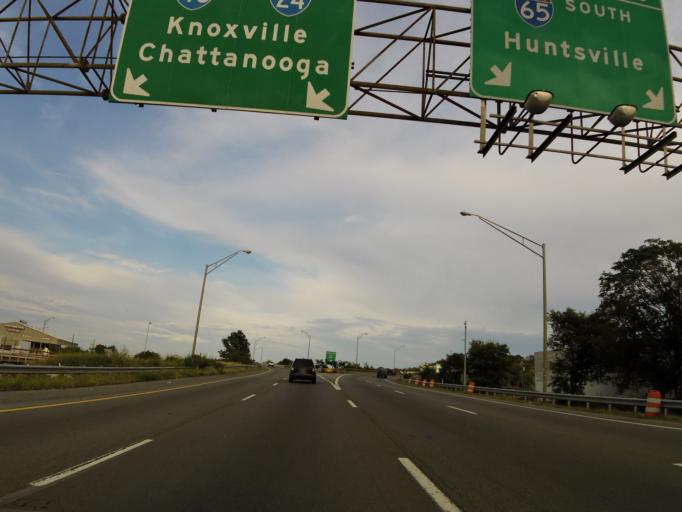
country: US
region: Tennessee
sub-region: Davidson County
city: Nashville
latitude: 36.1484
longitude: -86.7805
